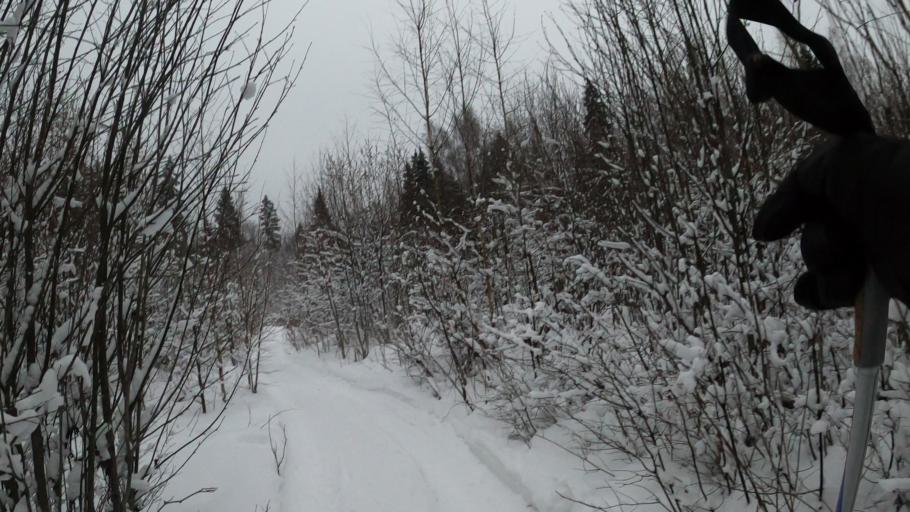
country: RU
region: Moskovskaya
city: Firsanovka
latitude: 55.9083
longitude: 37.2022
